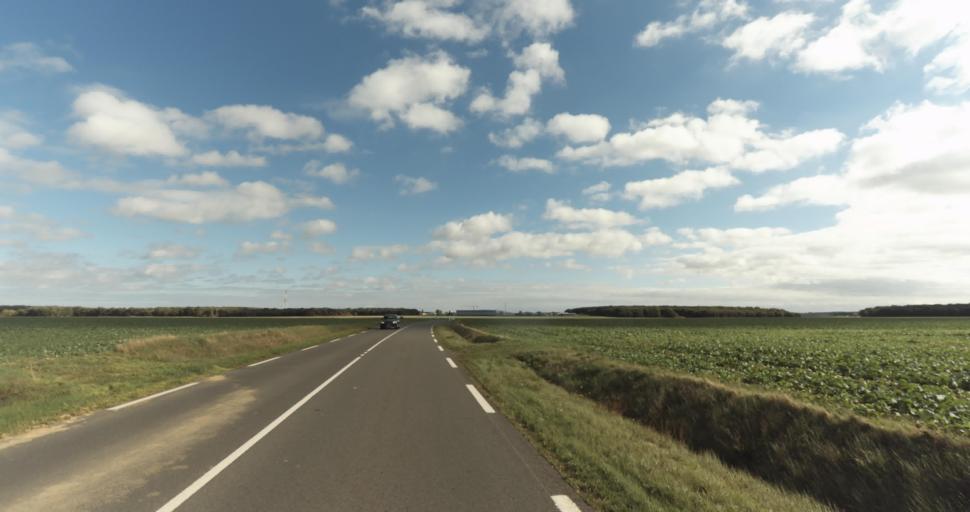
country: FR
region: Centre
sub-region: Departement d'Eure-et-Loir
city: Garnay
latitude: 48.7244
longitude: 1.3055
